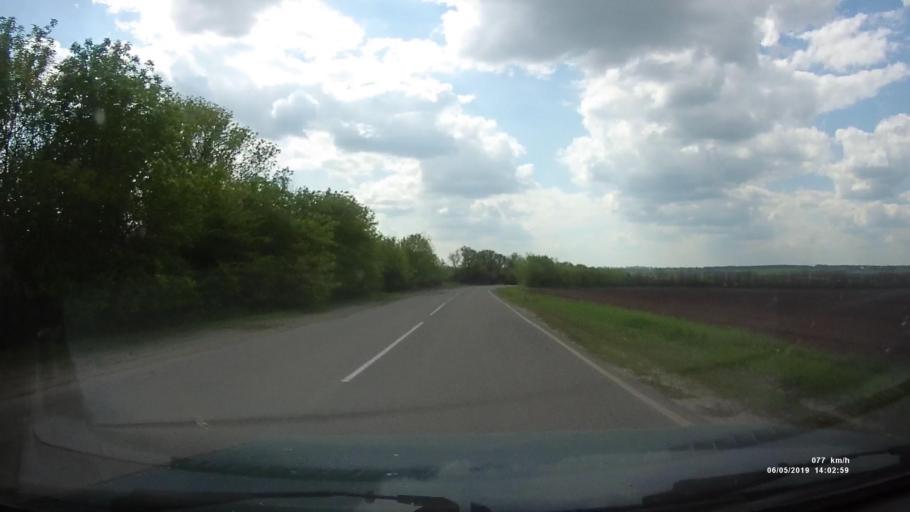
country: RU
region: Rostov
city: Shakhty
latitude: 47.6810
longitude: 40.3540
